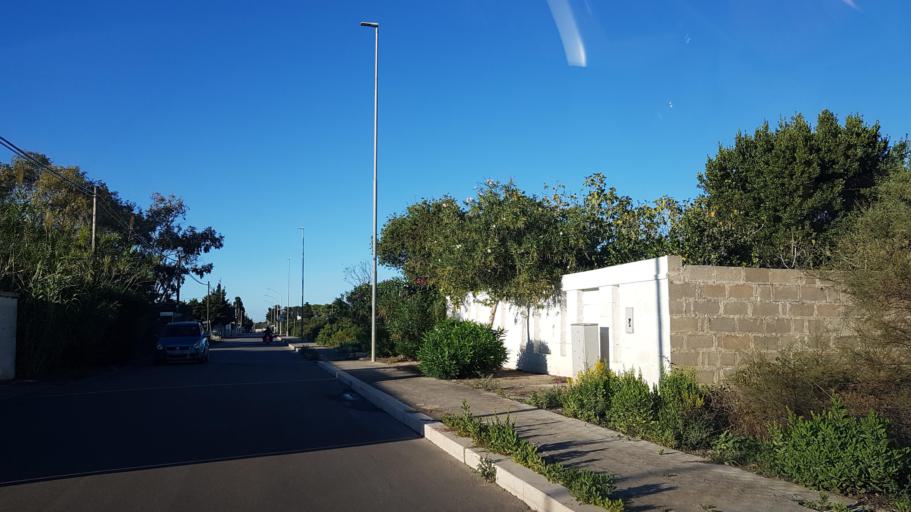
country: IT
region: Apulia
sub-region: Provincia di Lecce
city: Giorgilorio
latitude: 40.4596
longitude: 18.1951
